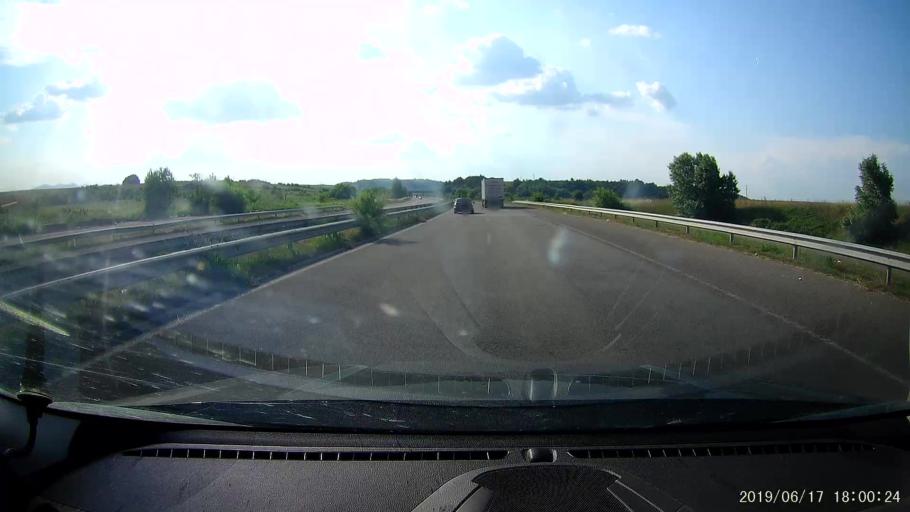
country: BG
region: Khaskovo
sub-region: Obshtina Svilengrad
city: Svilengrad
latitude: 41.7362
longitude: 26.2800
